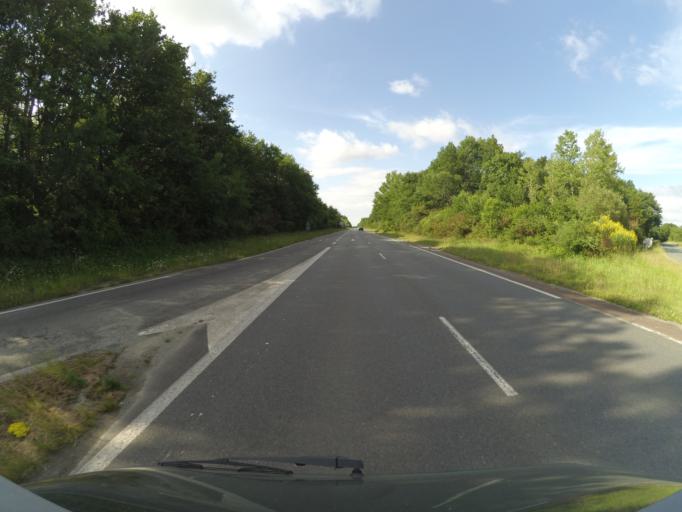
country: FR
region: Poitou-Charentes
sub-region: Departement de la Charente-Maritime
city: Le Gua
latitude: 45.7850
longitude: -0.9362
